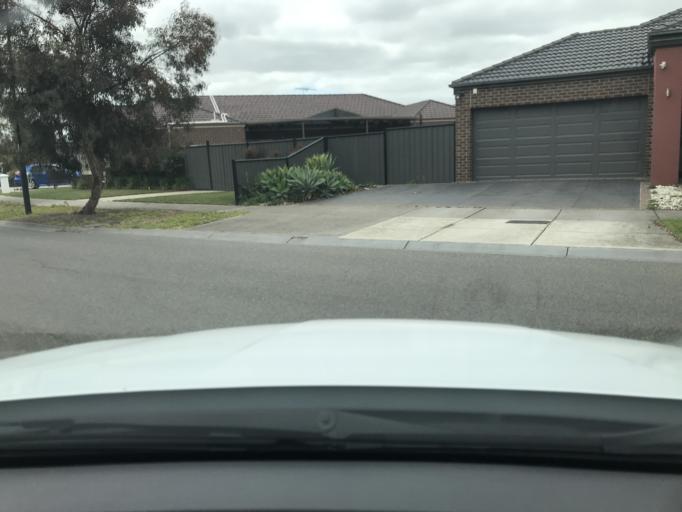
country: AU
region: Victoria
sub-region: Hume
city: Craigieburn
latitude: -37.5808
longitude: 144.9260
